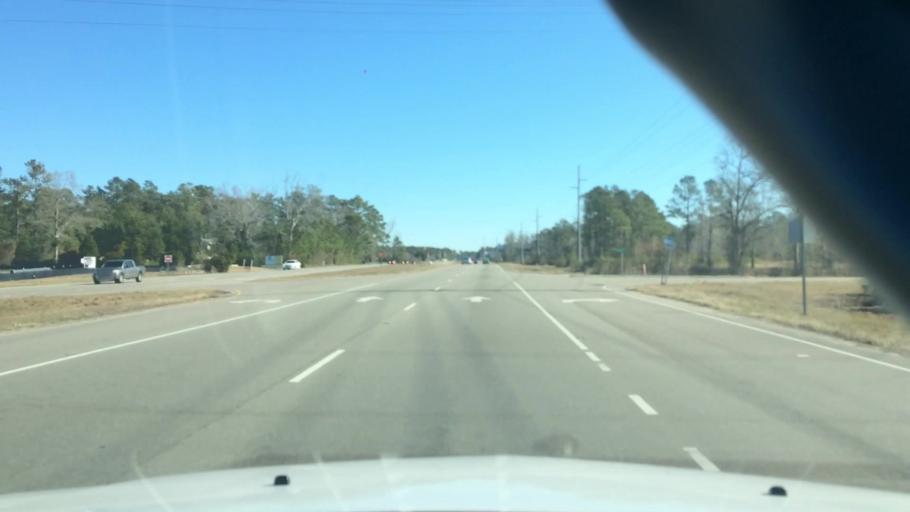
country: US
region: North Carolina
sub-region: Brunswick County
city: Shallotte
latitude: 34.0140
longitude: -78.2817
